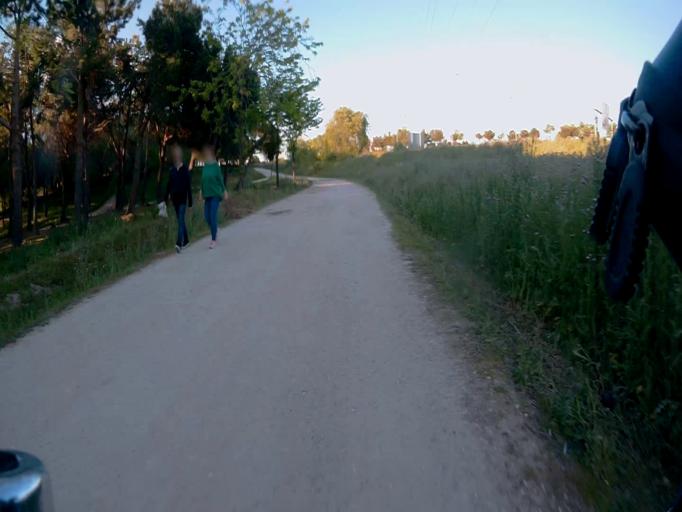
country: ES
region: Madrid
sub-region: Provincia de Madrid
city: Leganes
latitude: 40.3217
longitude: -3.7895
